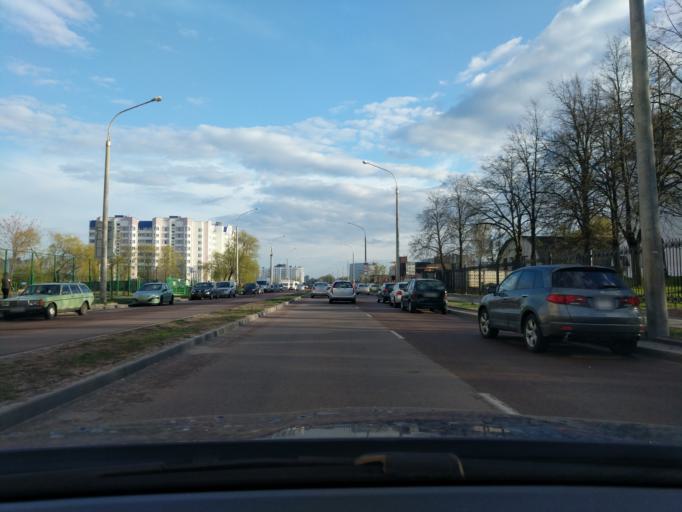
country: BY
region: Minsk
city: Novoye Medvezhino
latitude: 53.9069
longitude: 27.4731
